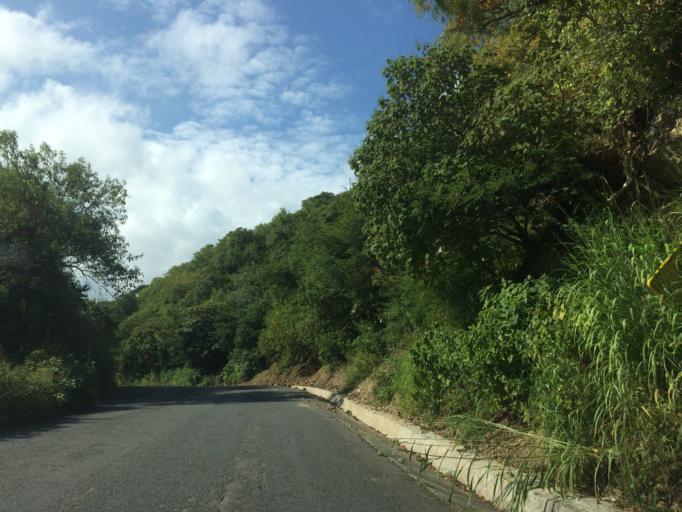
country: MX
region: Nayarit
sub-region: Ahuacatlan
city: Ahuacatlan
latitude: 21.0174
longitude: -104.4758
